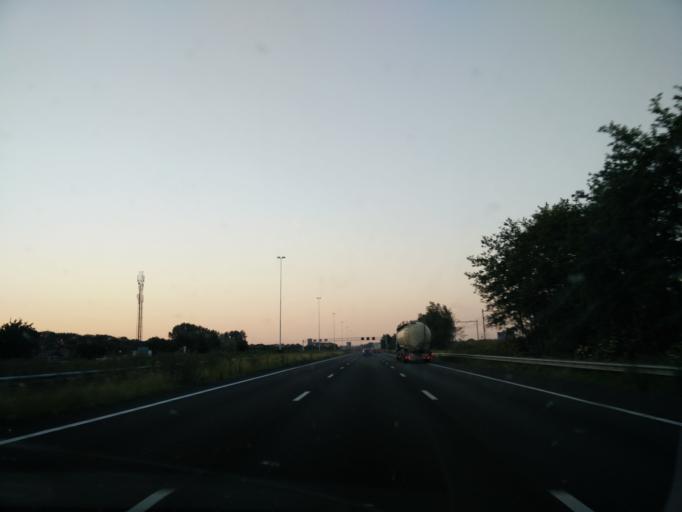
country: NL
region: South Holland
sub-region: Gemeente Zwijndrecht
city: Zwijndrecht
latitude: 51.7426
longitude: 4.6373
